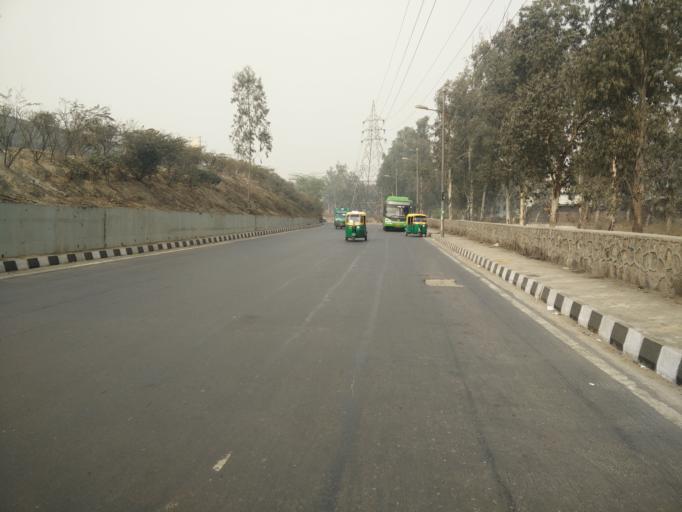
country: IN
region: Uttar Pradesh
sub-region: Gautam Buddha Nagar
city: Noida
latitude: 28.6512
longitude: 77.3196
